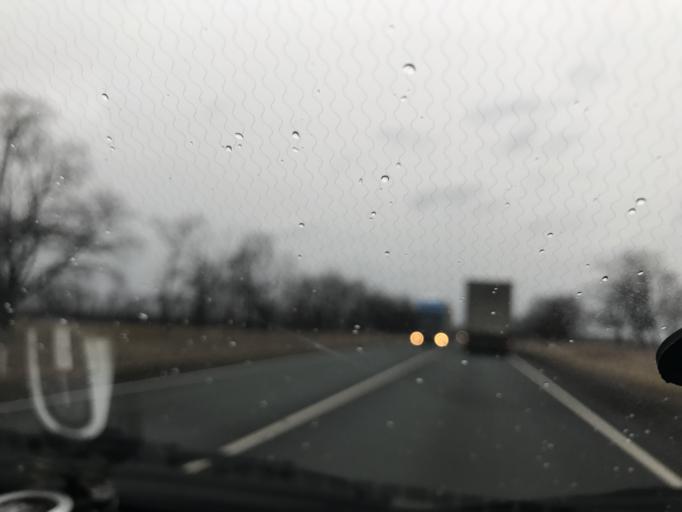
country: RU
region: Krasnodarskiy
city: Novoleushkovskaya
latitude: 46.0258
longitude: 39.9971
